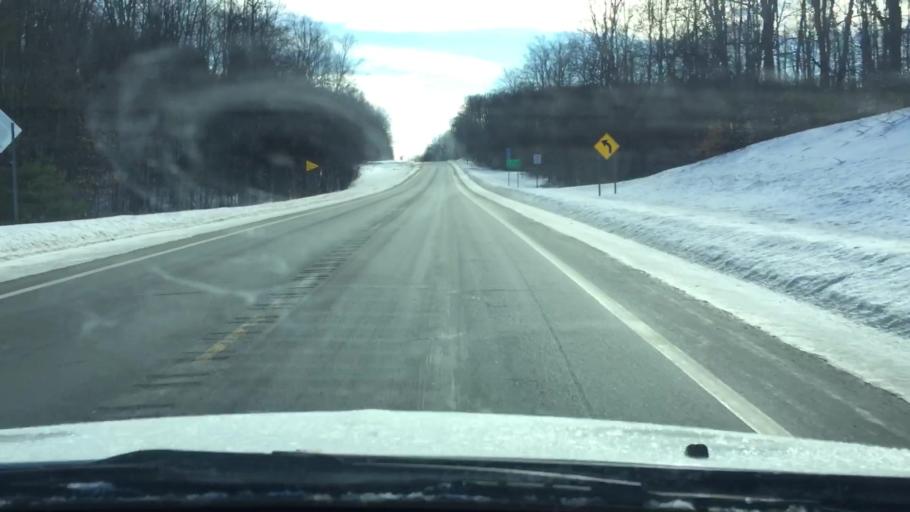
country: US
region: Michigan
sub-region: Antrim County
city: Mancelona
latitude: 44.9773
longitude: -85.0543
